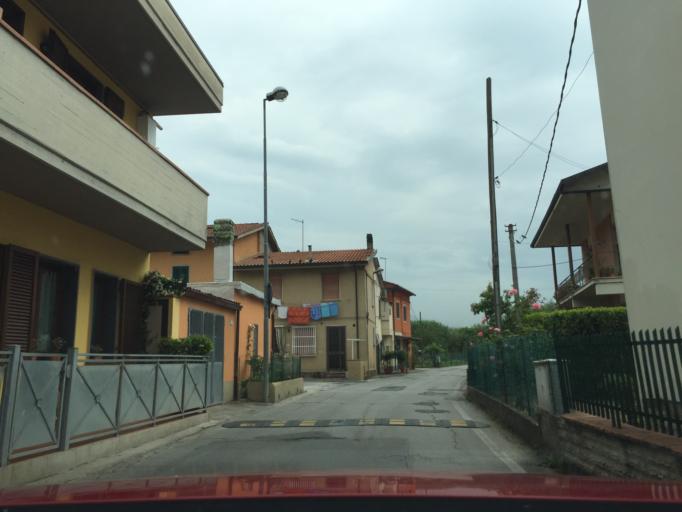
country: IT
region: Tuscany
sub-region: Provincia di Pistoia
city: Pieve a Nievole
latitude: 43.8797
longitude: 10.8090
